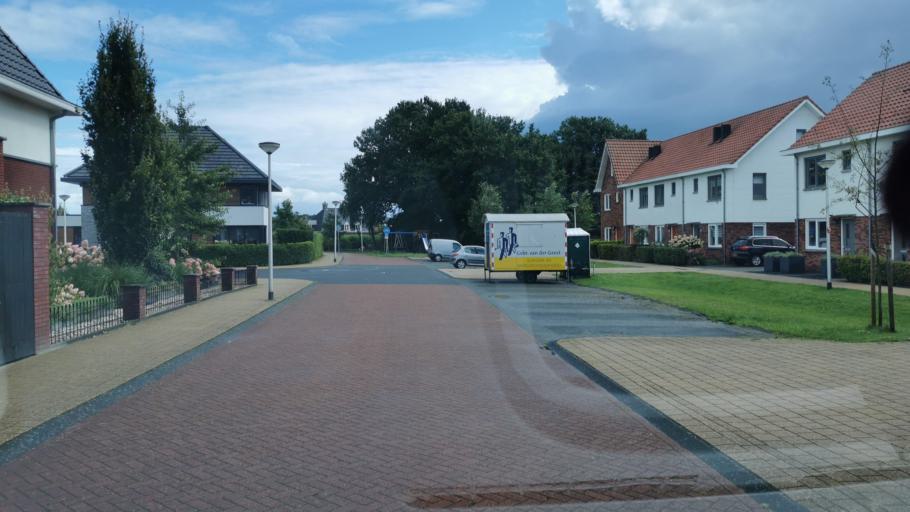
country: NL
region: Overijssel
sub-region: Gemeente Losser
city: Losser
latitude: 52.2683
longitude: 7.0045
